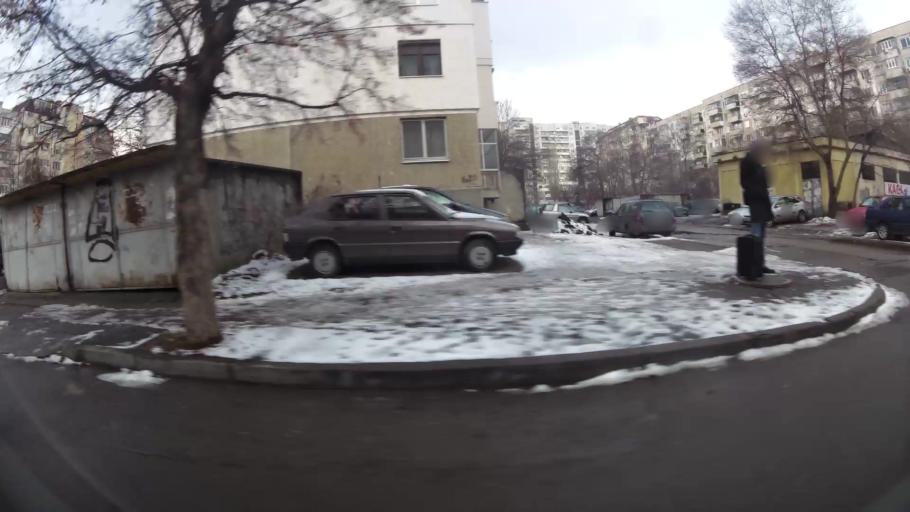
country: BG
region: Sofia-Capital
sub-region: Stolichna Obshtina
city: Sofia
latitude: 42.6968
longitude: 23.2905
